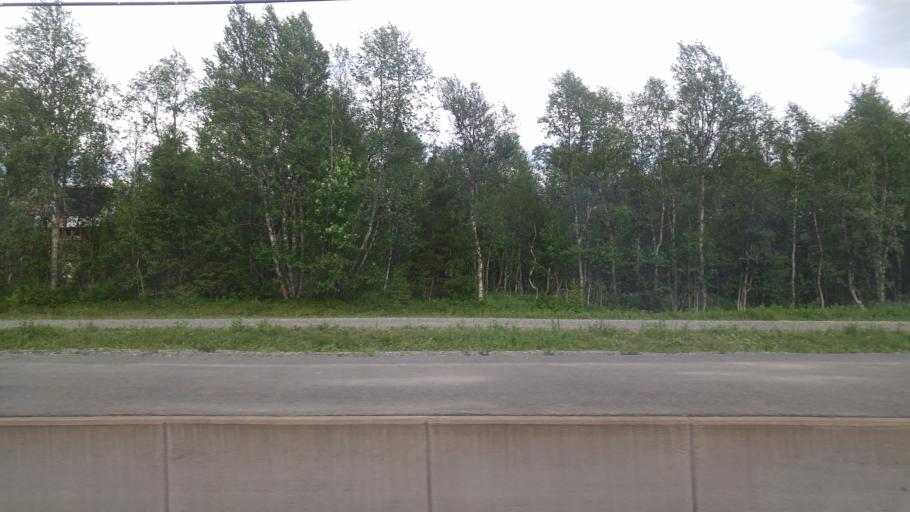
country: NO
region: Nord-Trondelag
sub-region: Meraker
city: Meraker
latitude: 63.2901
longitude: 12.3355
